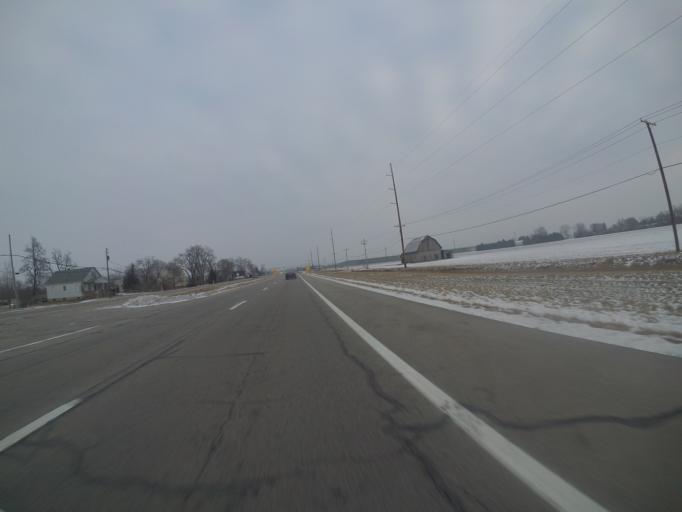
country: US
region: Ohio
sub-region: Wood County
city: Walbridge
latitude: 41.5637
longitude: -83.5326
